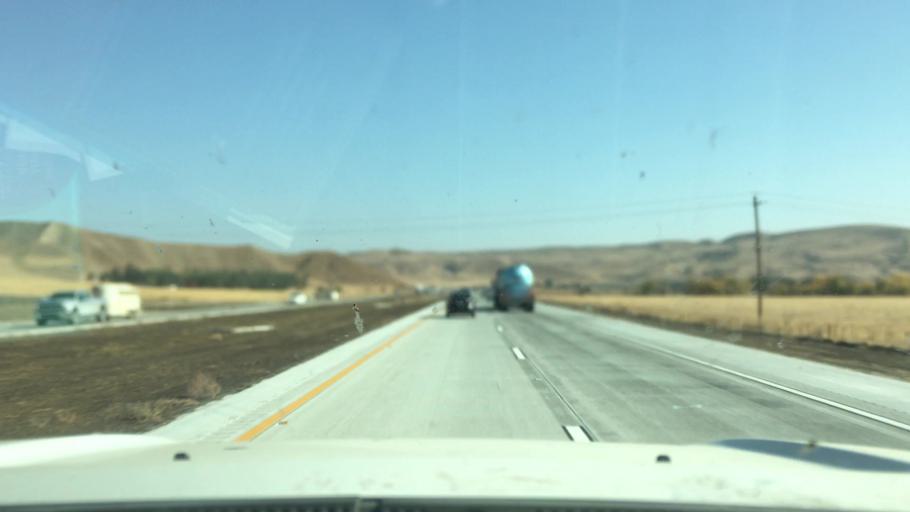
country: US
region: California
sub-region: San Luis Obispo County
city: Shandon
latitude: 35.6625
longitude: -120.3805
